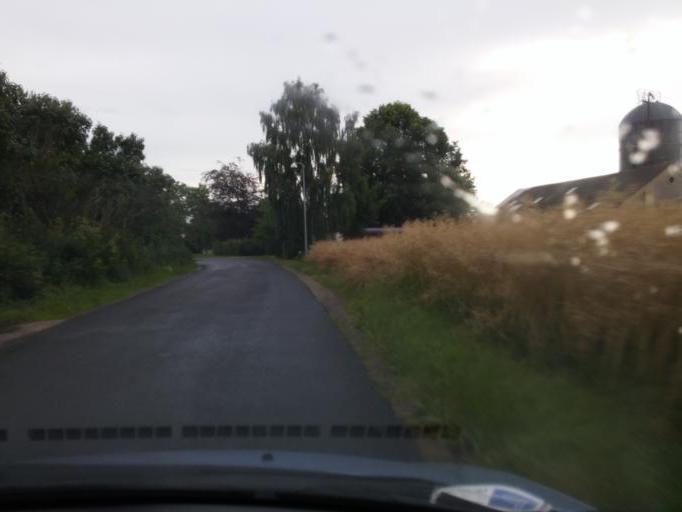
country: DK
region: South Denmark
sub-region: Kerteminde Kommune
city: Langeskov
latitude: 55.4075
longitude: 10.5810
